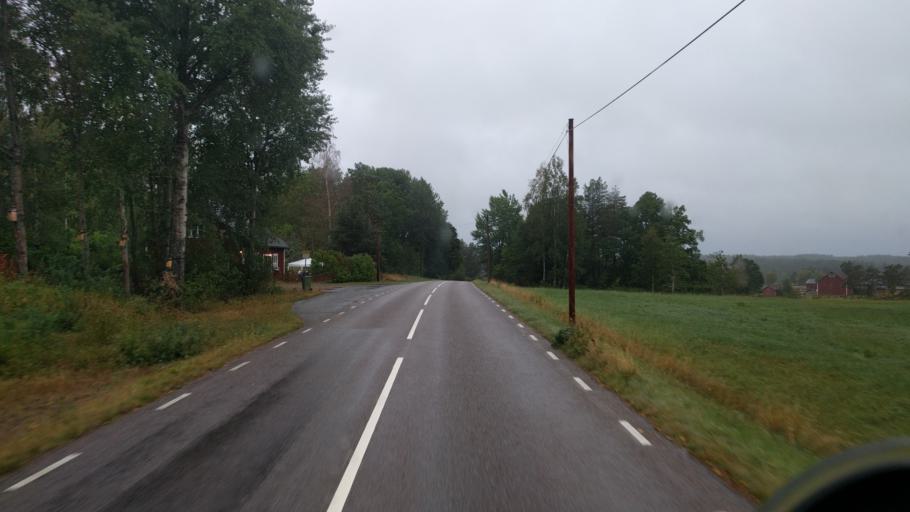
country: SE
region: Kalmar
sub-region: Vasterviks Kommun
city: Gamleby
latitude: 57.7914
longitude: 16.4118
